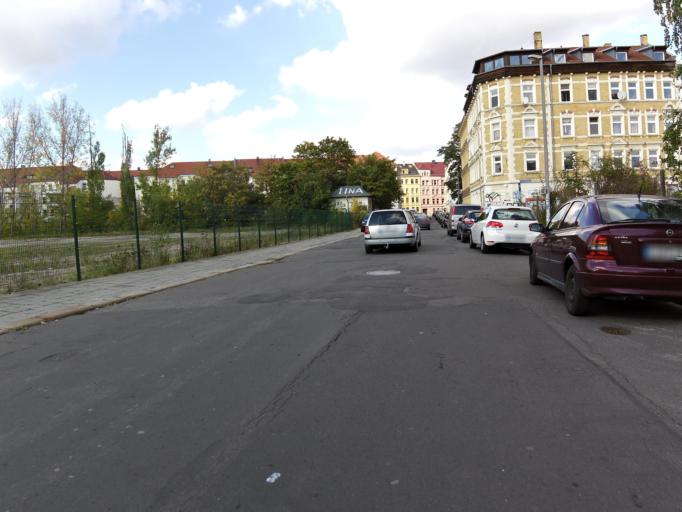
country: DE
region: Saxony
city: Leipzig
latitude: 51.3306
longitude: 12.3265
